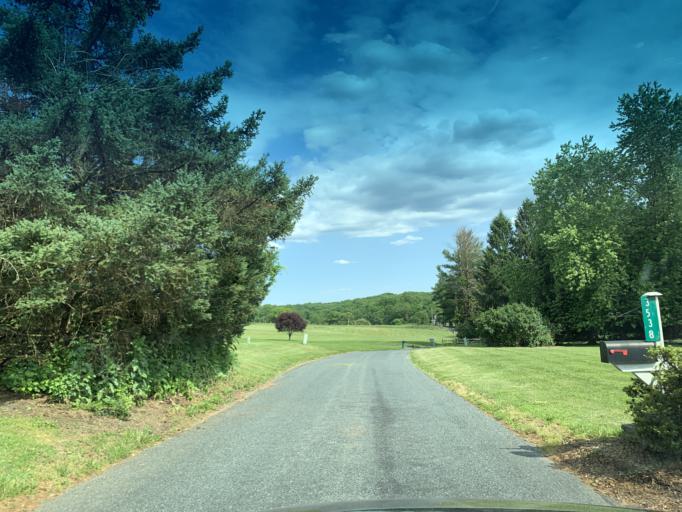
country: US
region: Maryland
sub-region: Harford County
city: Jarrettsville
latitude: 39.6018
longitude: -76.4580
